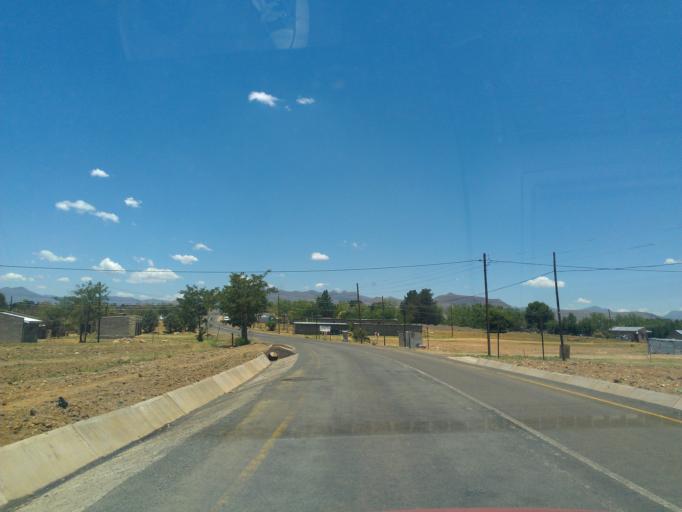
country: LS
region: Berea
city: Teyateyaneng
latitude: -29.1042
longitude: 27.9613
